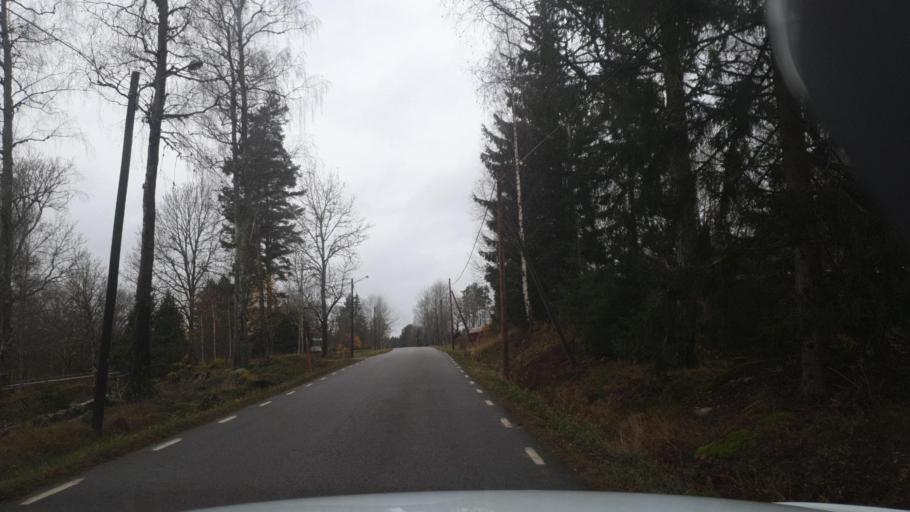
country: SE
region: Vaermland
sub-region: Arvika Kommun
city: Arvika
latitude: 59.5727
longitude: 12.5042
